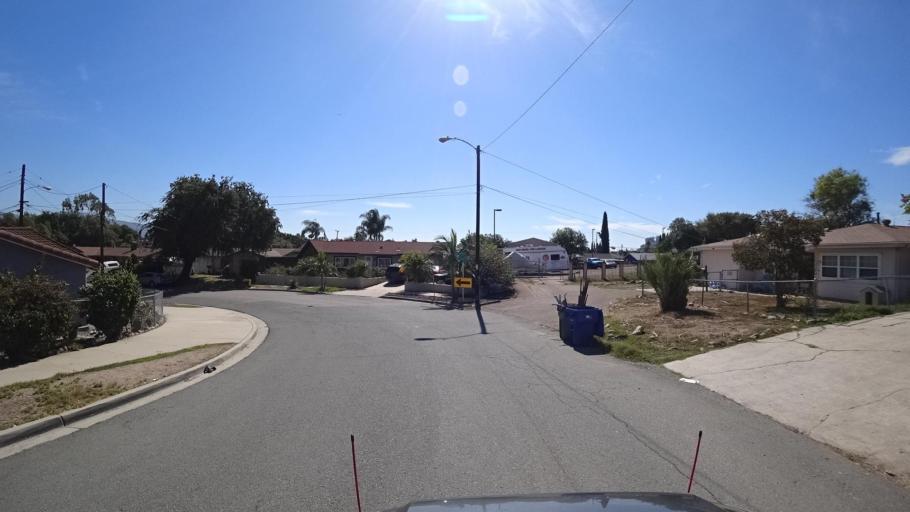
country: US
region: California
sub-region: San Diego County
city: La Presa
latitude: 32.7103
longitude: -117.0061
